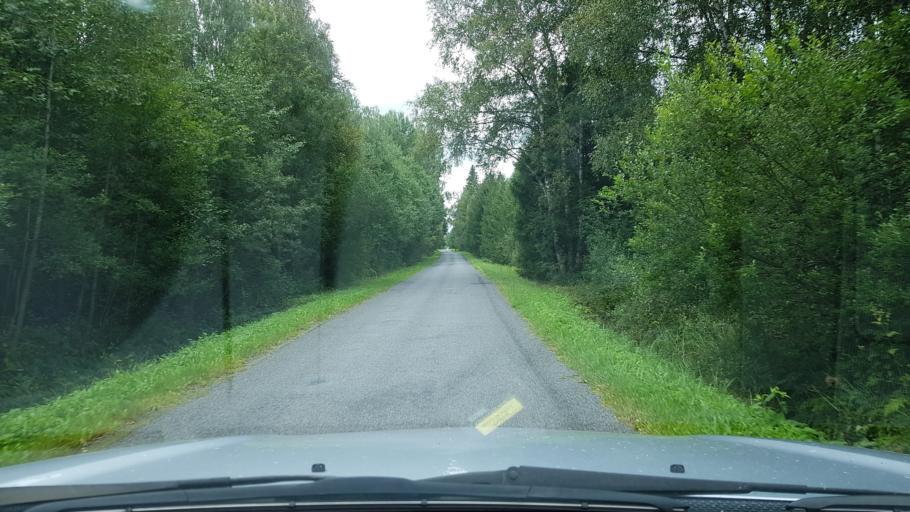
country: EE
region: Harju
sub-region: Rae vald
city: Vaida
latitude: 59.2978
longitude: 24.9961
